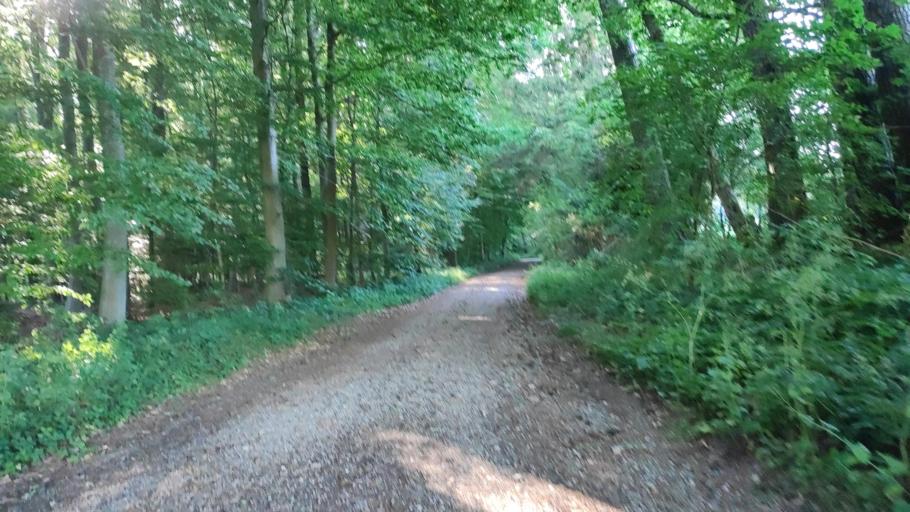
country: DE
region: Bavaria
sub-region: Swabia
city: Horgau
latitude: 48.3777
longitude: 10.7127
